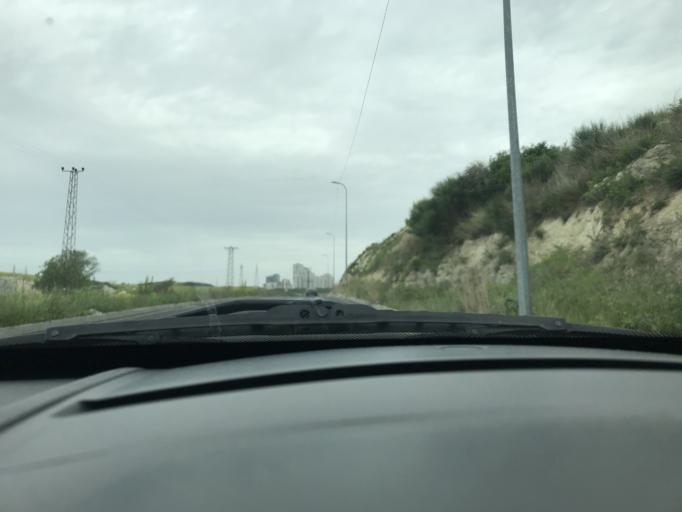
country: TR
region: Istanbul
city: Esenyurt
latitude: 41.0931
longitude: 28.6806
